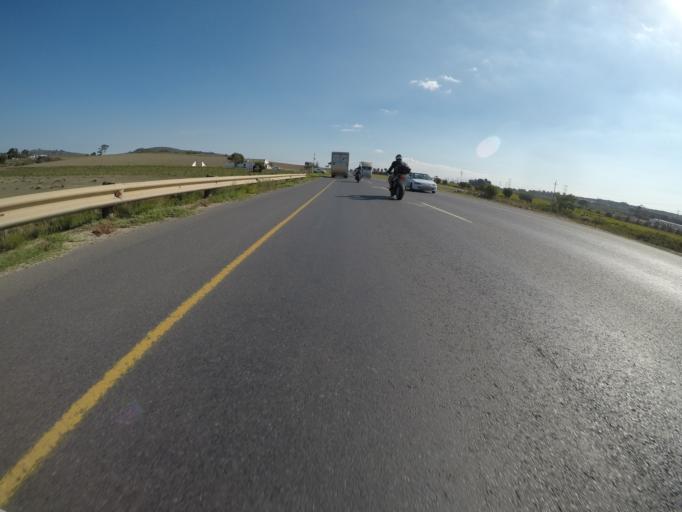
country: ZA
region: Western Cape
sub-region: City of Cape Town
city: Kraaifontein
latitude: -33.8902
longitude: 18.7423
